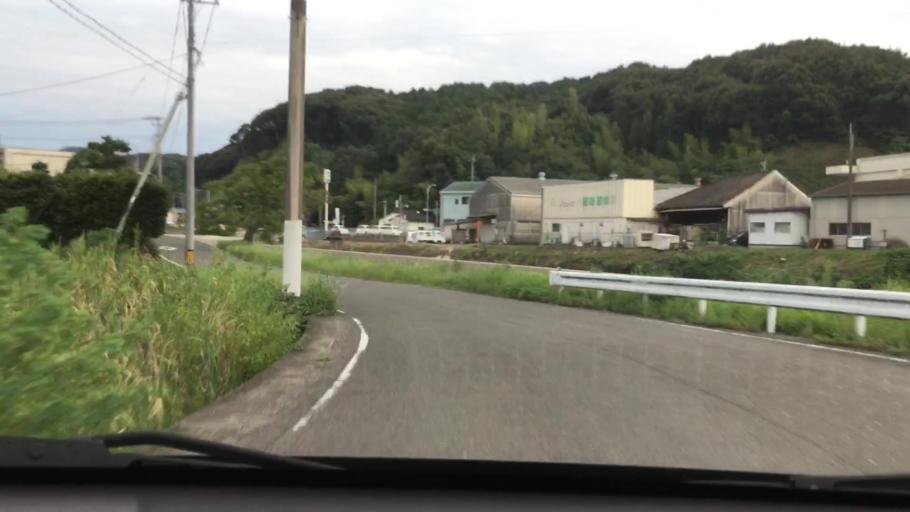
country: JP
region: Nagasaki
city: Togitsu
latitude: 32.9886
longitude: 129.7734
